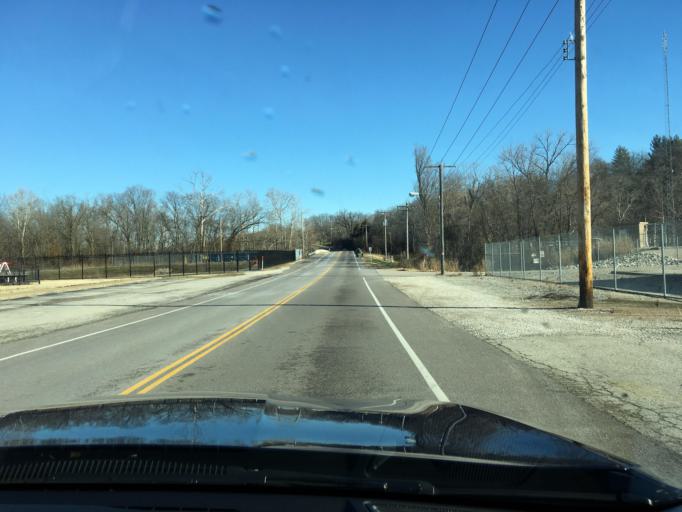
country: US
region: Missouri
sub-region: Jefferson County
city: De Soto
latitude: 38.1486
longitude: -90.5501
